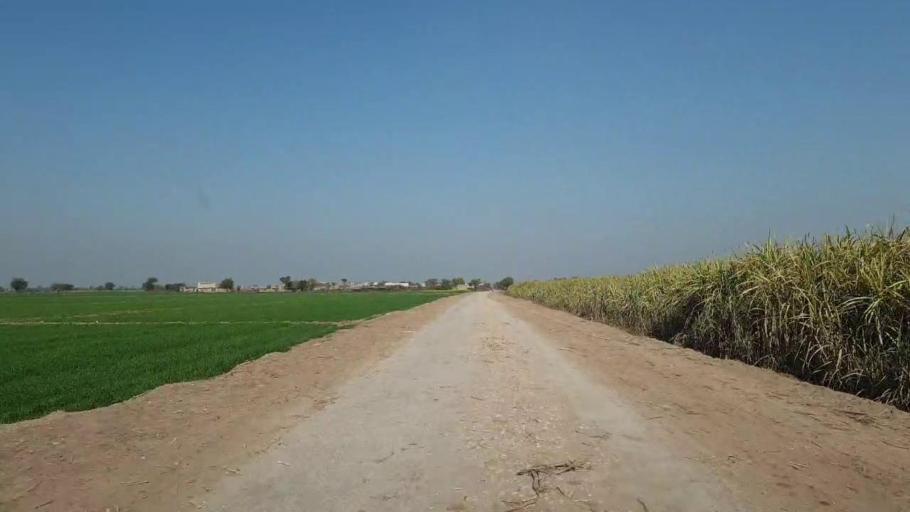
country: PK
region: Sindh
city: Shahdadpur
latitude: 25.9484
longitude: 68.5111
